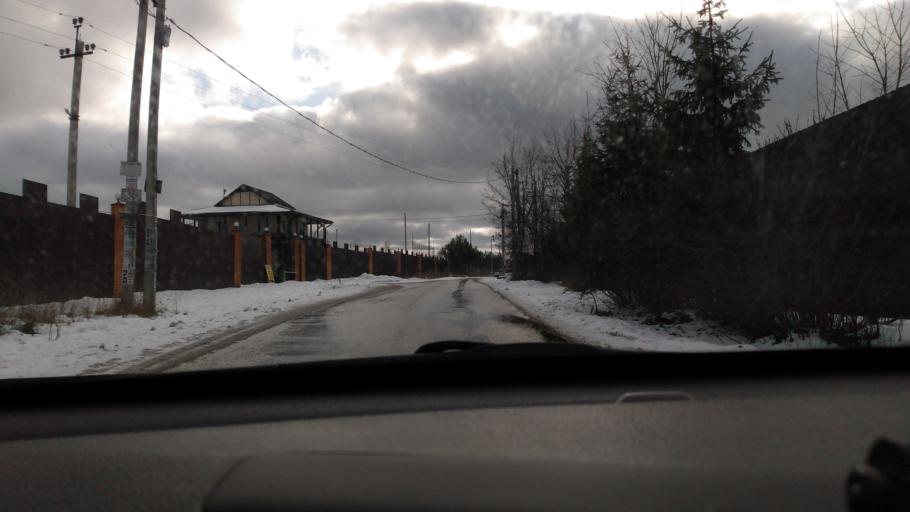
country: RU
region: Moskovskaya
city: Troitsk
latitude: 55.4843
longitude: 37.2702
